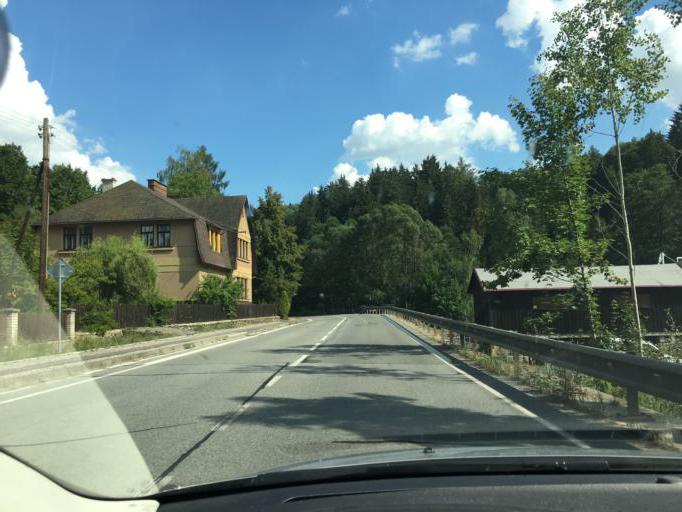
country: CZ
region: Liberecky
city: Semily
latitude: 50.5959
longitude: 15.3616
